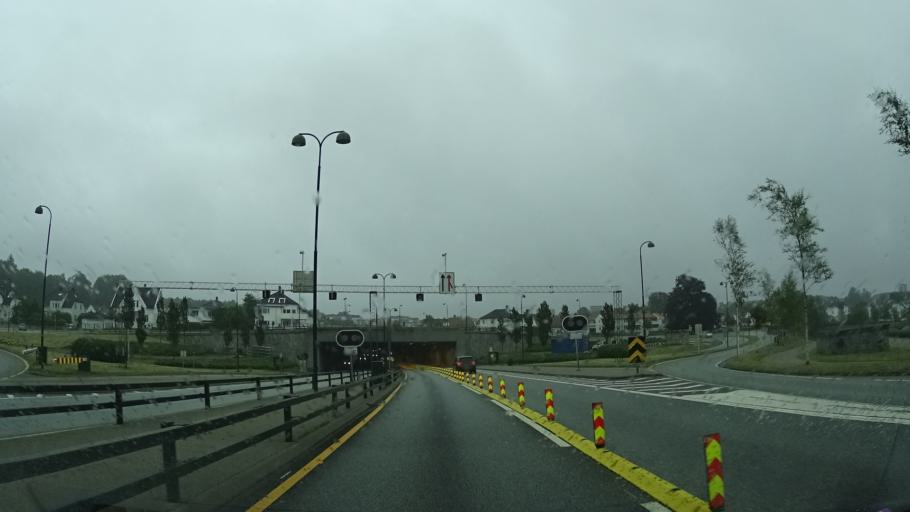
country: NO
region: Vest-Agder
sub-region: Kristiansand
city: Kristiansand
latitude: 58.1551
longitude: 8.0002
